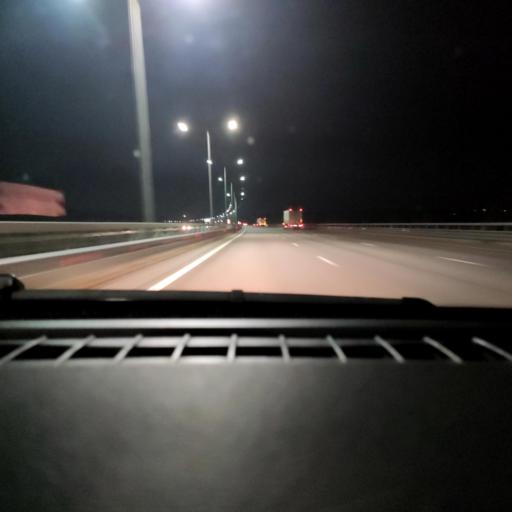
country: RU
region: Voronezj
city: Somovo
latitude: 51.7846
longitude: 39.2889
